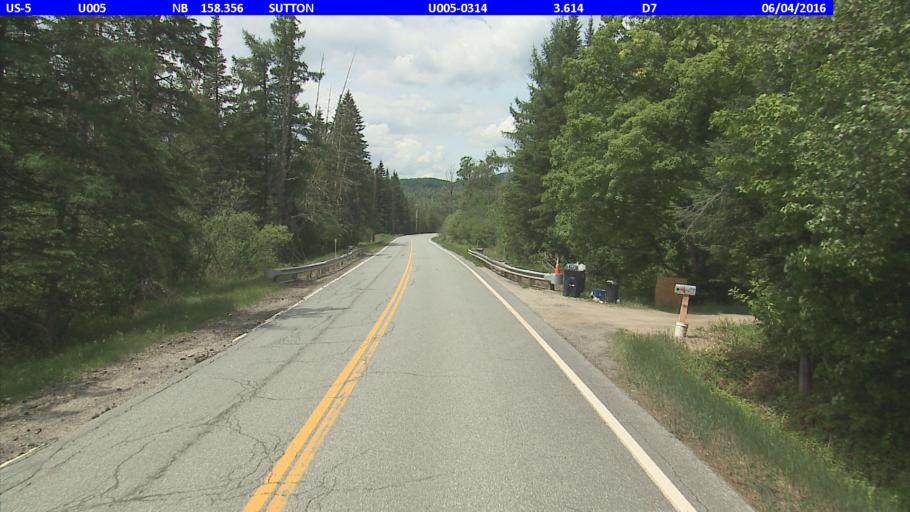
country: US
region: Vermont
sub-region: Caledonia County
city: Lyndonville
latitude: 44.6777
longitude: -72.0317
